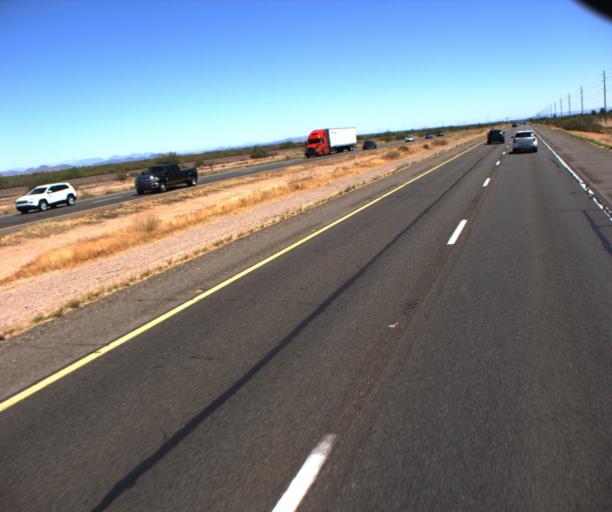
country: US
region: Arizona
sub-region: Maricopa County
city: Sun City West
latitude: 33.7185
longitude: -112.4527
